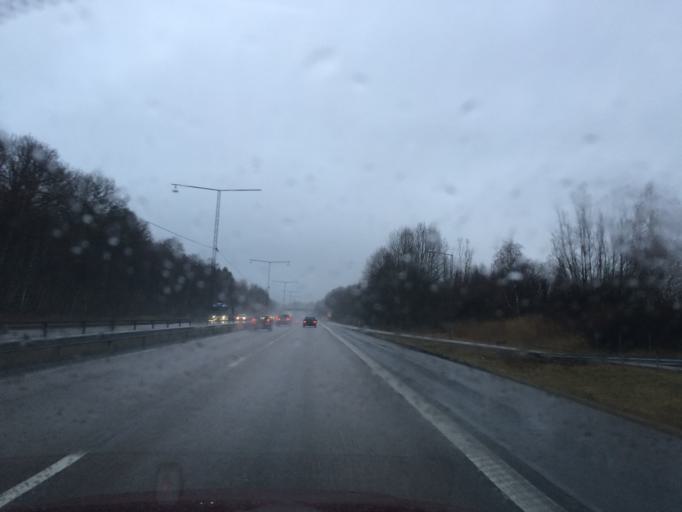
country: SE
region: Vaestra Goetaland
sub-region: Molndal
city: Lindome
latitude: 57.5748
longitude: 12.0598
